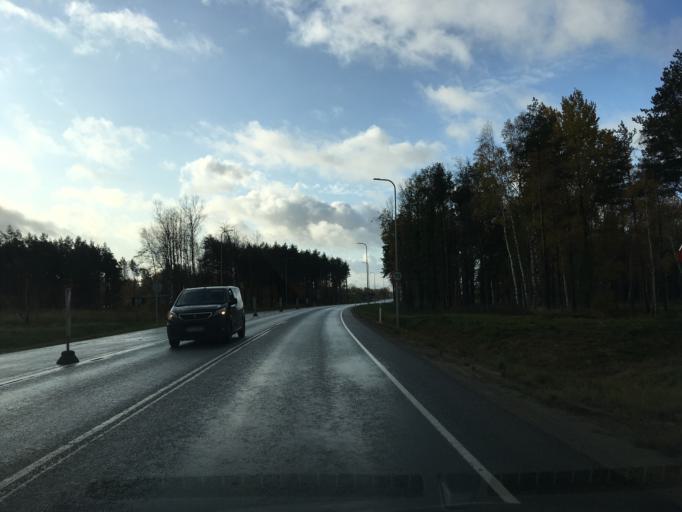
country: EE
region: Harju
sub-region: Saue vald
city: Laagri
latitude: 59.3576
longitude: 24.6005
